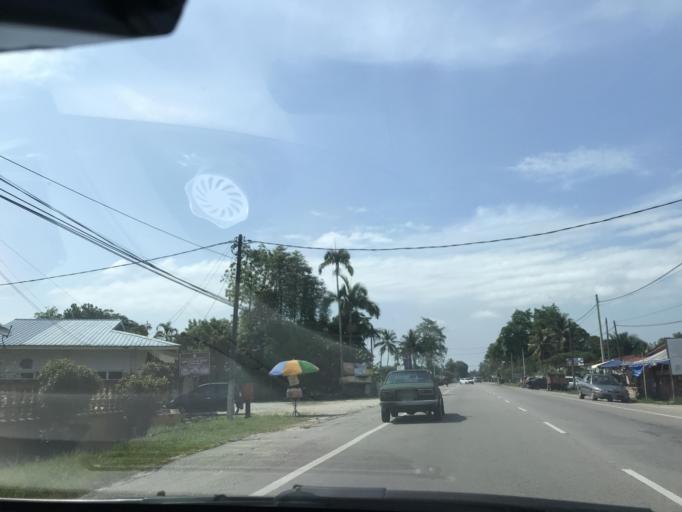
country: MY
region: Kelantan
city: Tumpat
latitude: 6.1471
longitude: 102.1632
